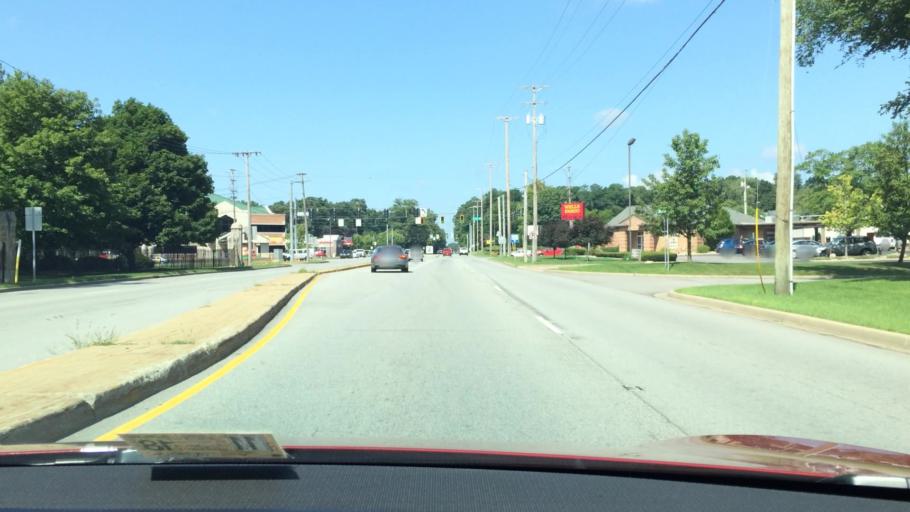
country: US
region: Indiana
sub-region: Saint Joseph County
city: Georgetown
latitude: 41.7239
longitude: -86.1862
